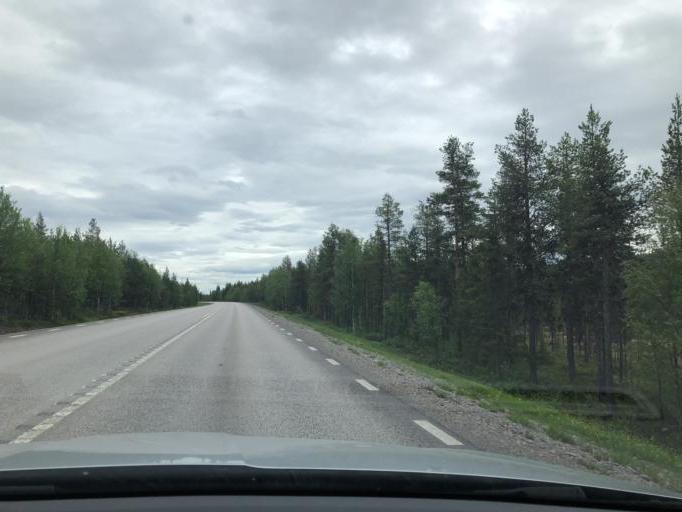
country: SE
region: Norrbotten
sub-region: Gallivare Kommun
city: Malmberget
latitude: 67.6448
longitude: 21.1220
